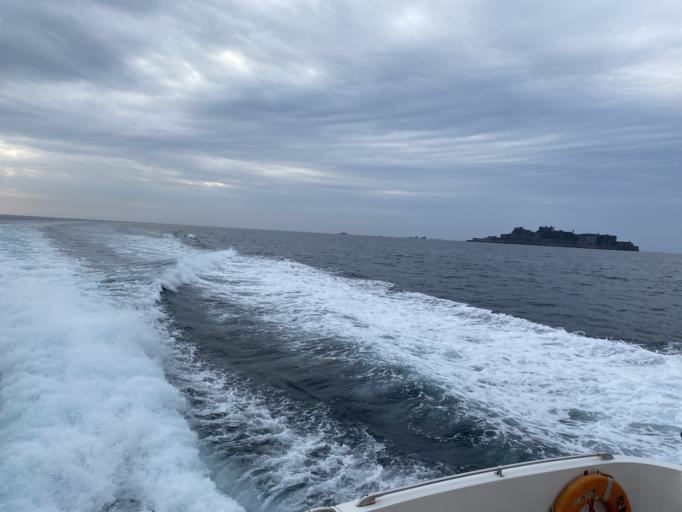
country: JP
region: Nagasaki
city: Nagasaki-shi
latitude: 32.6289
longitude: 129.7539
